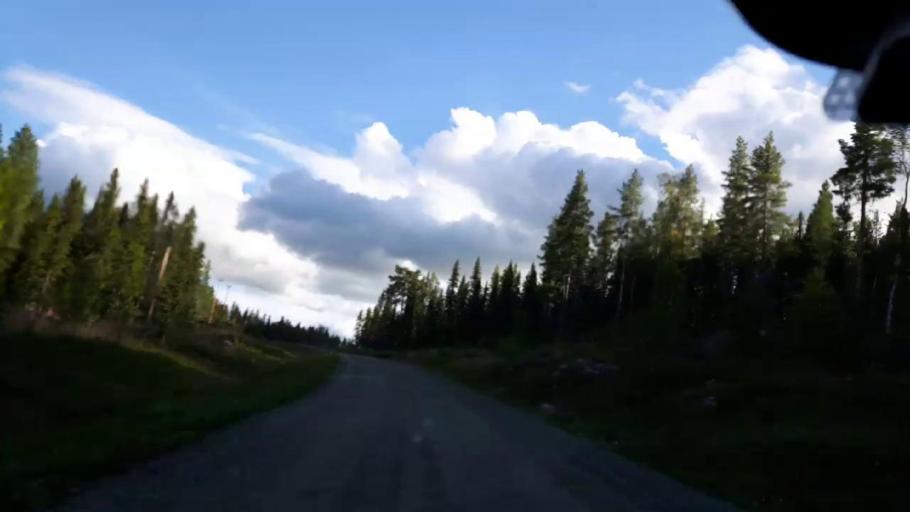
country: SE
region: Jaemtland
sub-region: Stroemsunds Kommun
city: Stroemsund
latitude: 63.3422
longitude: 15.5663
